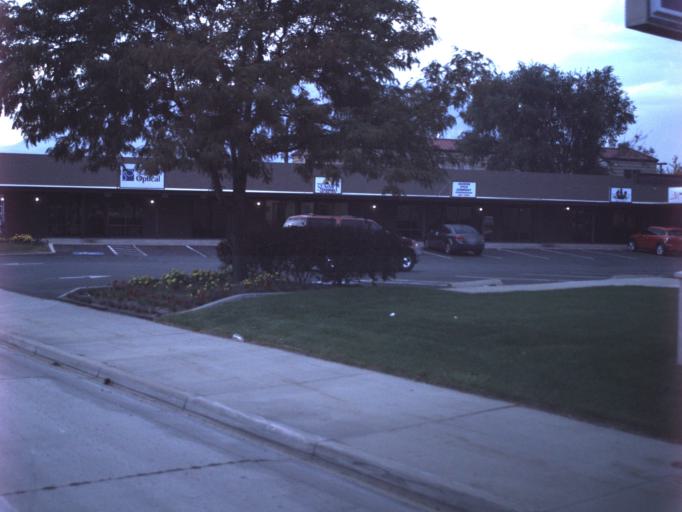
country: US
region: Utah
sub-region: Utah County
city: Orem
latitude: 40.2701
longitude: -111.6830
